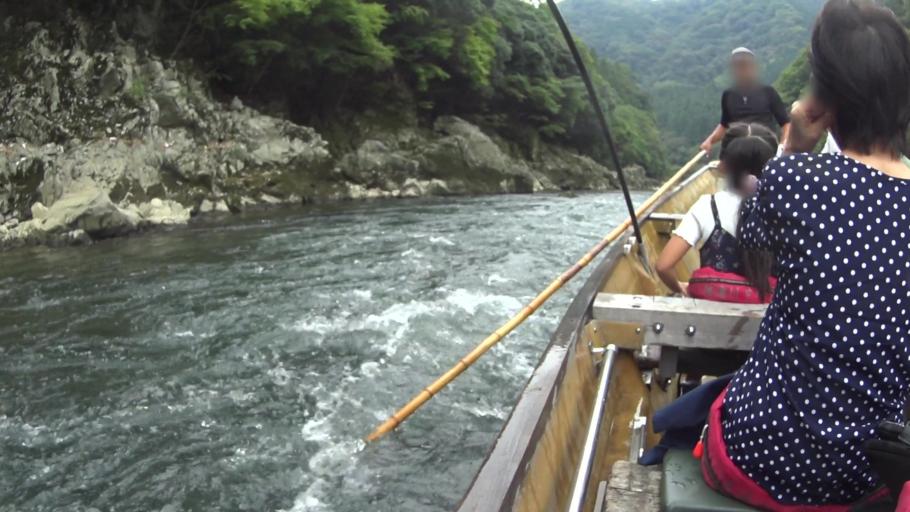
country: JP
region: Kyoto
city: Kameoka
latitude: 35.0216
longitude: 135.6221
